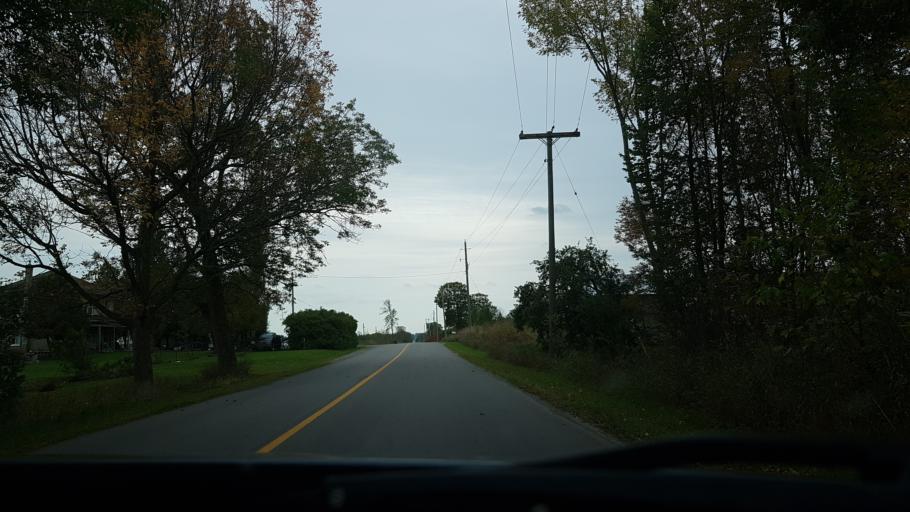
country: CA
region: Ontario
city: Orillia
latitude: 44.6280
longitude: -78.9545
